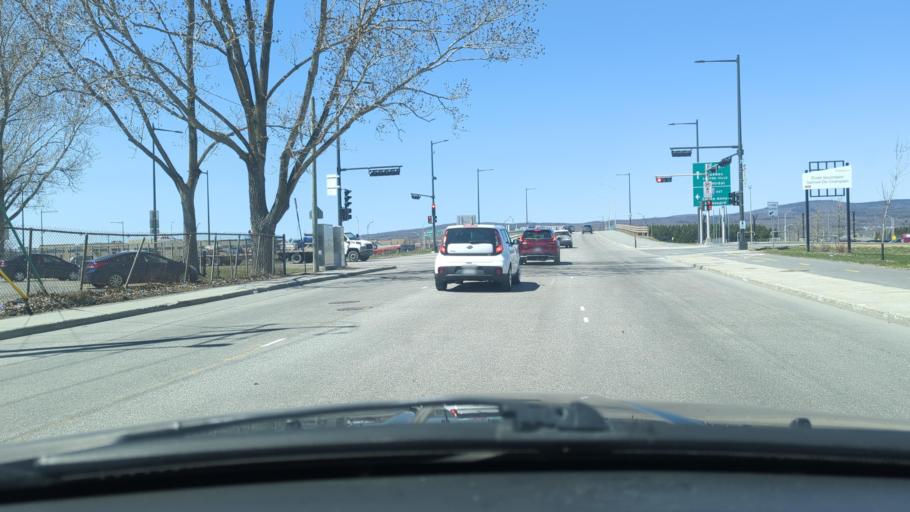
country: CA
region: Quebec
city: Quebec
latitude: 46.8600
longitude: -71.2109
